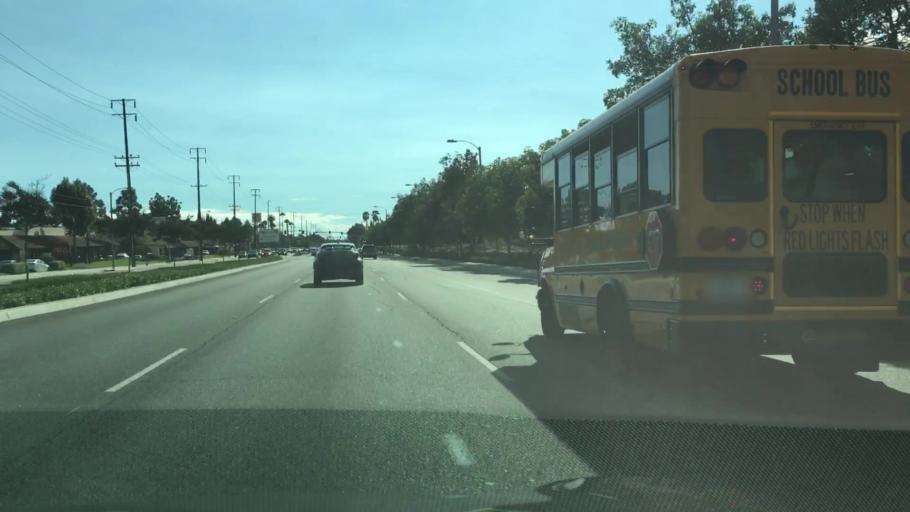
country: US
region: California
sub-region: Los Angeles County
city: East La Mirada
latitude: 33.8989
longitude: -117.9857
